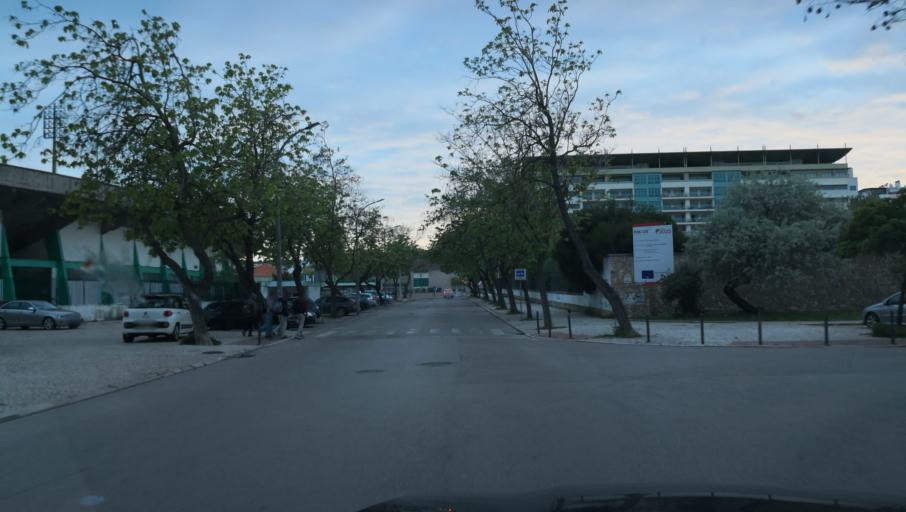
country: PT
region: Setubal
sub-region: Setubal
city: Setubal
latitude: 38.5328
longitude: -8.8908
